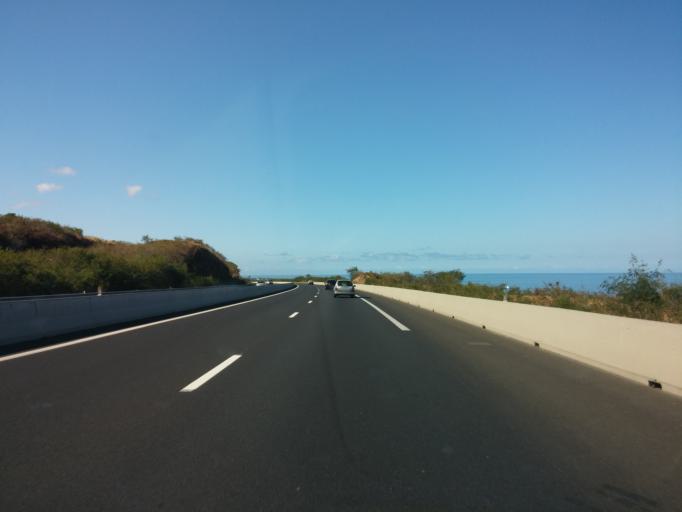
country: RE
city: Piton Saint-Leu
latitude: -21.2397
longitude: 55.3154
